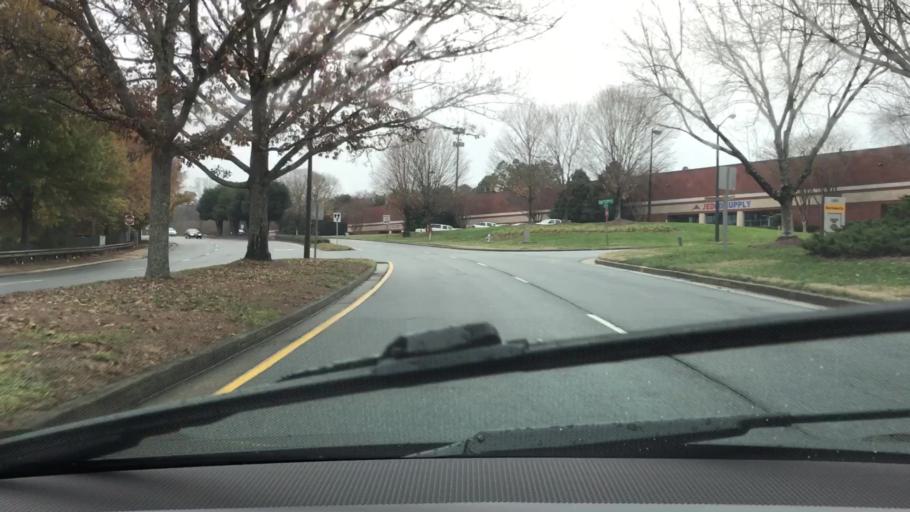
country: US
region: Georgia
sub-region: Gwinnett County
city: Suwanee
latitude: 34.0162
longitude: -84.0684
